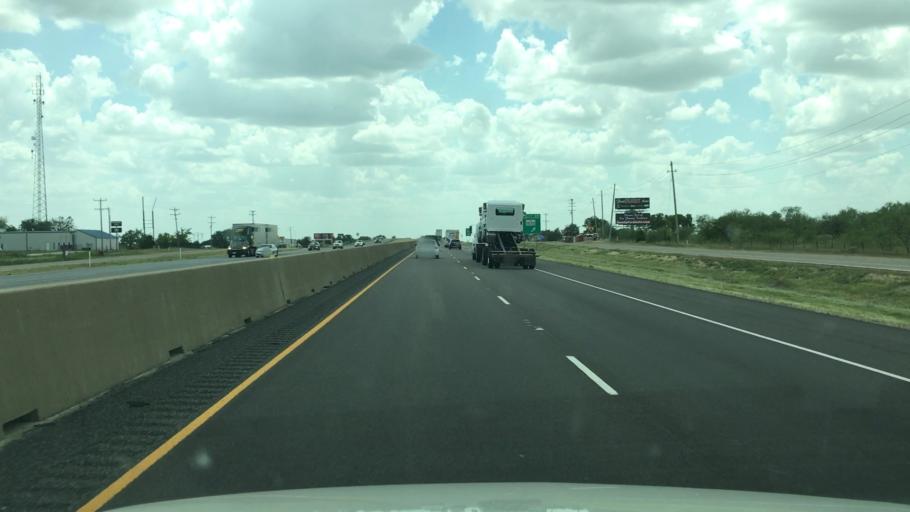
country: US
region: Texas
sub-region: Hunt County
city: Greenville
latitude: 33.0693
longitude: -96.1478
